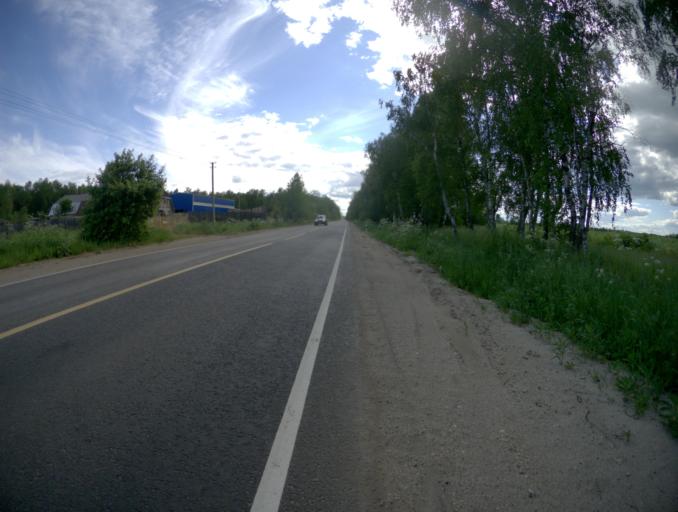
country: RU
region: Ivanovo
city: Kitovo
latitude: 56.8306
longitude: 41.3033
